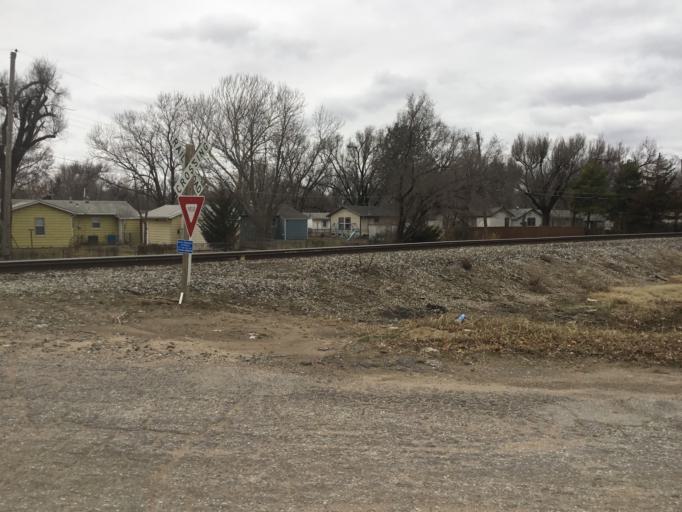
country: US
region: Kansas
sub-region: Sedgwick County
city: Wichita
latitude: 37.6608
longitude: -97.3755
